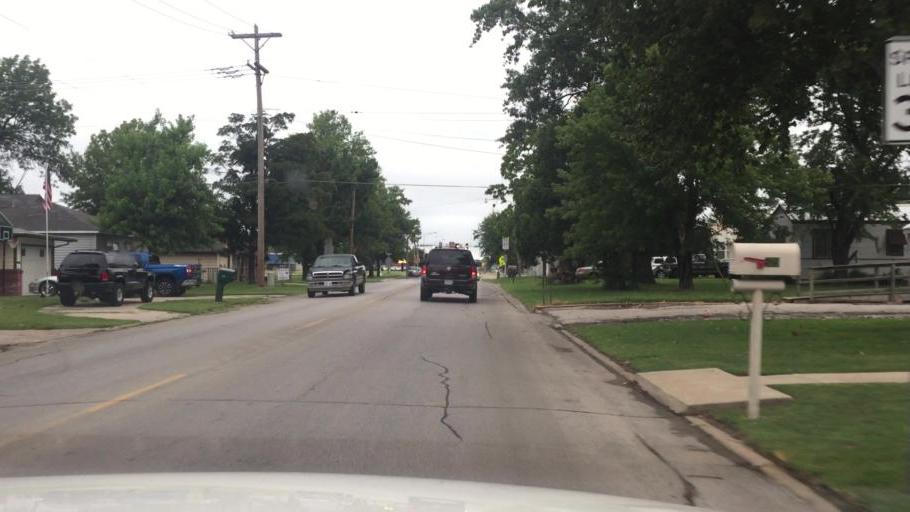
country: US
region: Kansas
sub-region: Montgomery County
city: Coffeyville
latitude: 37.0388
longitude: -95.6474
